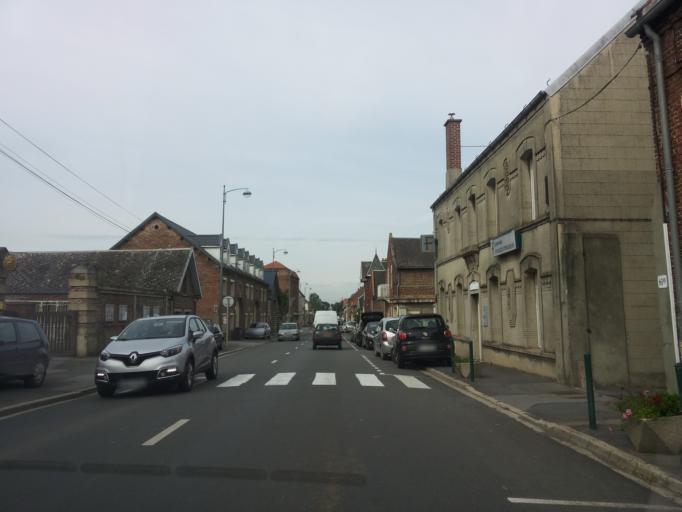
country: FR
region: Nord-Pas-de-Calais
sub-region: Departement du Pas-de-Calais
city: Marquion
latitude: 50.2115
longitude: 3.0846
